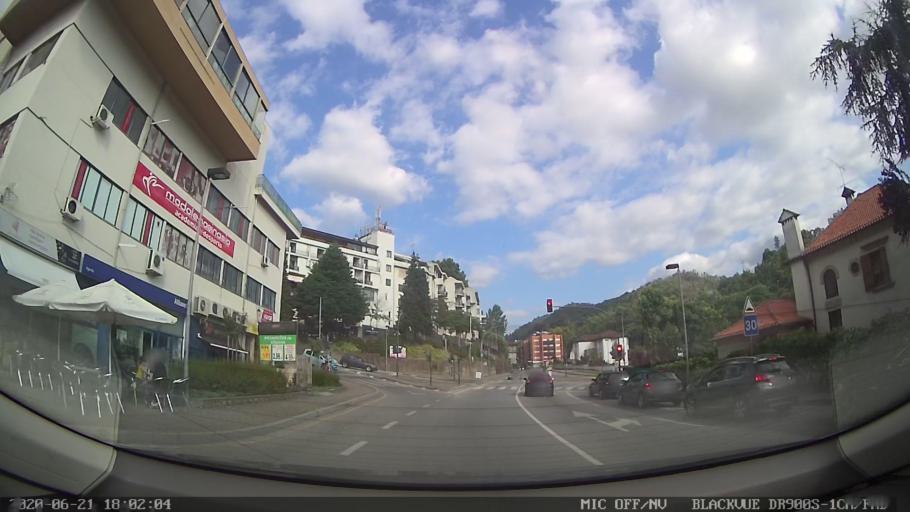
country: PT
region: Porto
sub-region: Amarante
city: Amarante
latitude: 41.2679
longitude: -8.0730
